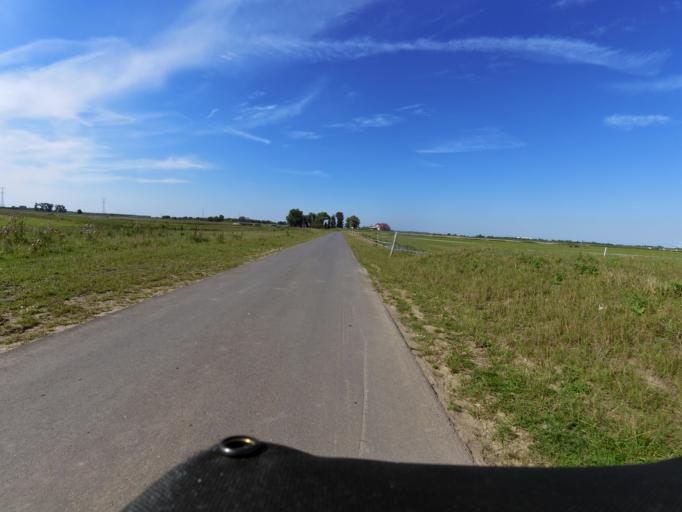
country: NL
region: South Holland
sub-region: Gemeente Hardinxveld-Giessendam
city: Neder-Hardinxveld
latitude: 51.7866
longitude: 4.8426
